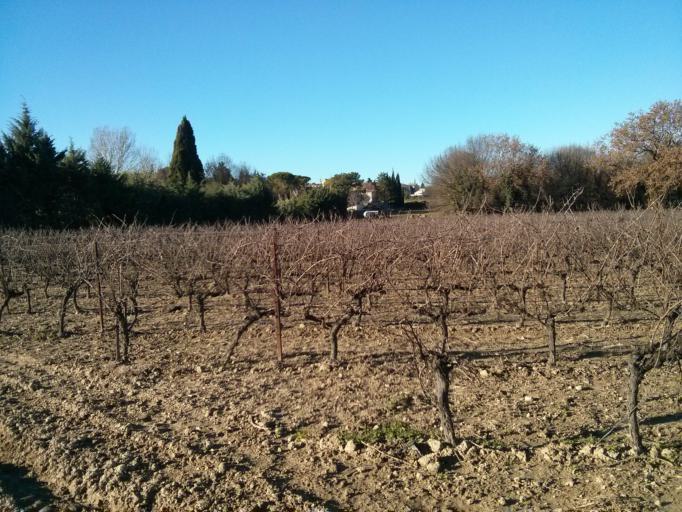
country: FR
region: Languedoc-Roussillon
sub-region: Departement du Gard
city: Aigues-Vives
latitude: 43.7413
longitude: 4.1870
